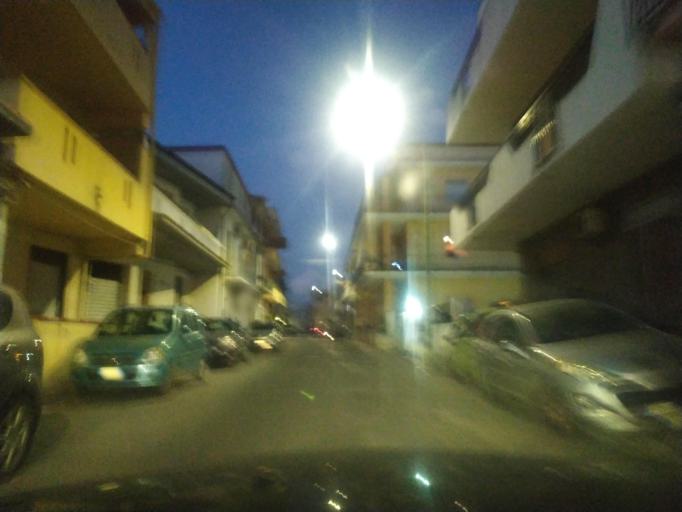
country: IT
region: Sicily
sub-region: Messina
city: Terme
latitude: 38.1382
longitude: 15.1626
